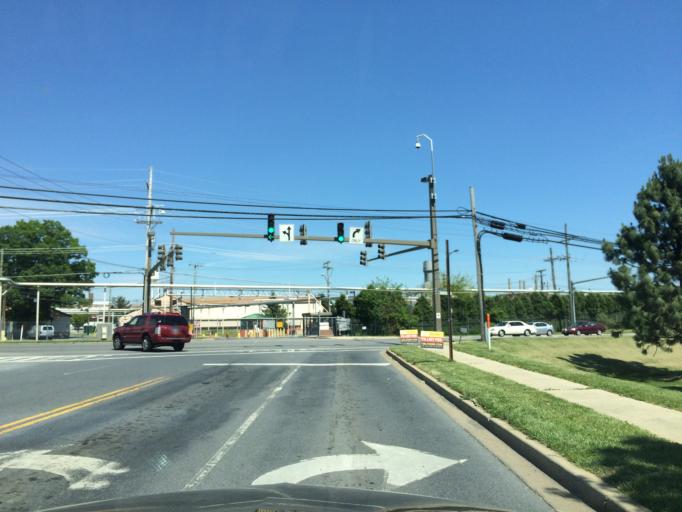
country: US
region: Maryland
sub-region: Frederick County
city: Clover Hill
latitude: 39.4324
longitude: -77.4351
